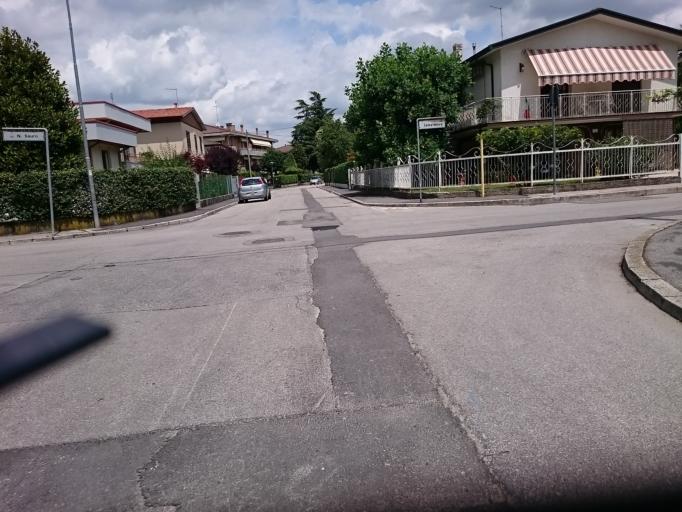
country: IT
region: Veneto
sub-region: Provincia di Padova
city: Caselle
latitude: 45.4130
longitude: 11.8226
